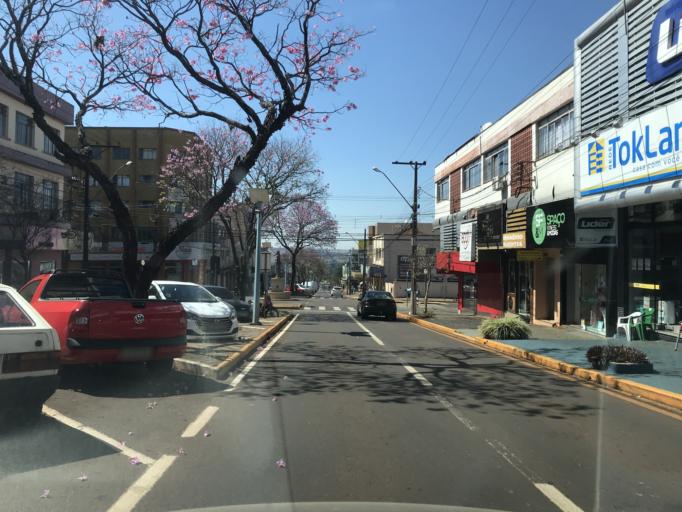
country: BR
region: Parana
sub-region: Toledo
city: Toledo
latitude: -24.7343
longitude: -53.7403
